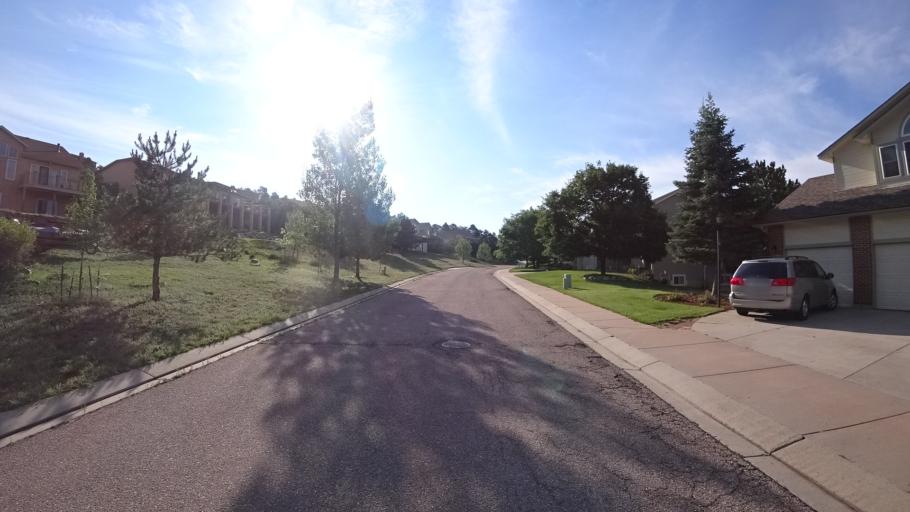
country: US
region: Colorado
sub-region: El Paso County
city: Air Force Academy
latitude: 38.9297
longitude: -104.8610
